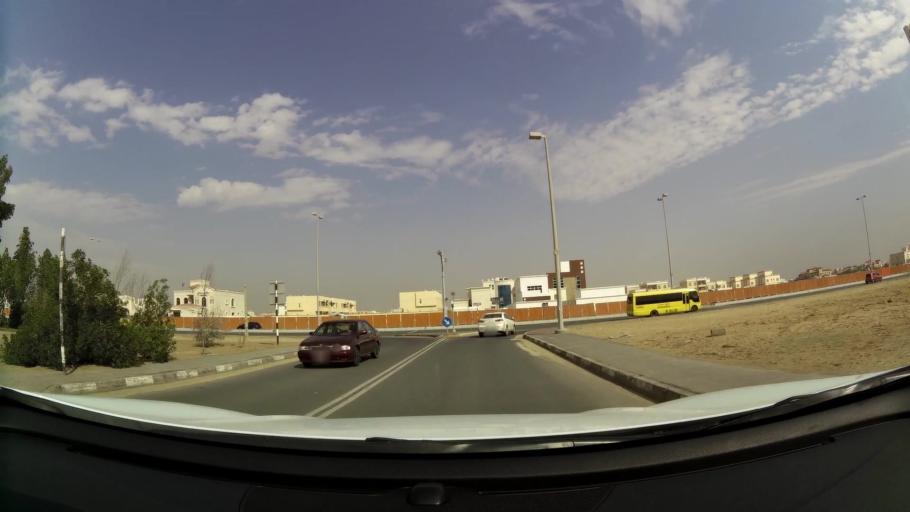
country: AE
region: Abu Dhabi
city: Abu Dhabi
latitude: 24.3336
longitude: 54.5382
